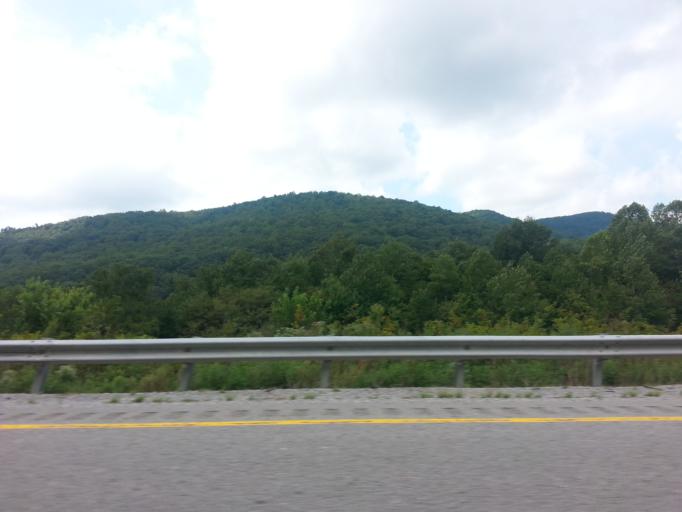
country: US
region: Tennessee
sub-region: Cumberland County
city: Fairfield Glade
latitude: 35.8928
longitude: -84.8416
